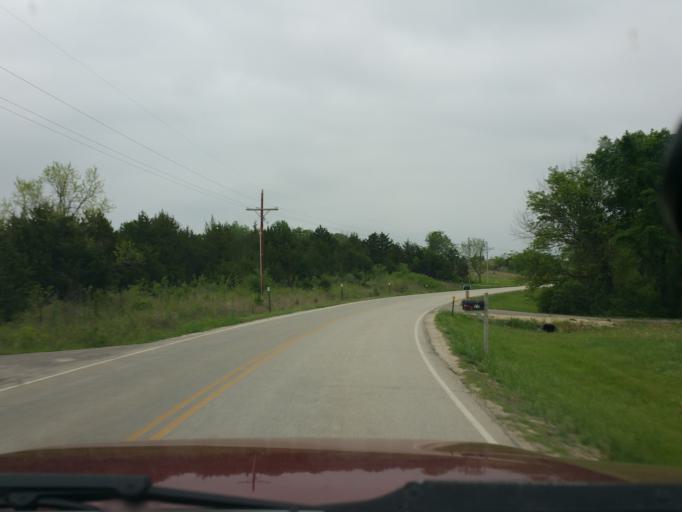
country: US
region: Kansas
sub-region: Riley County
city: Manhattan
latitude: 39.2637
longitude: -96.5705
